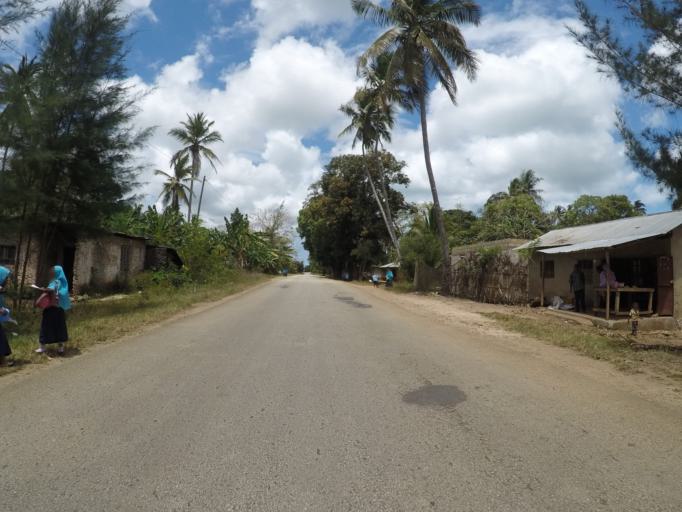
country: TZ
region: Zanzibar Central/South
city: Mahonda
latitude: -6.3082
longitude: 39.4319
